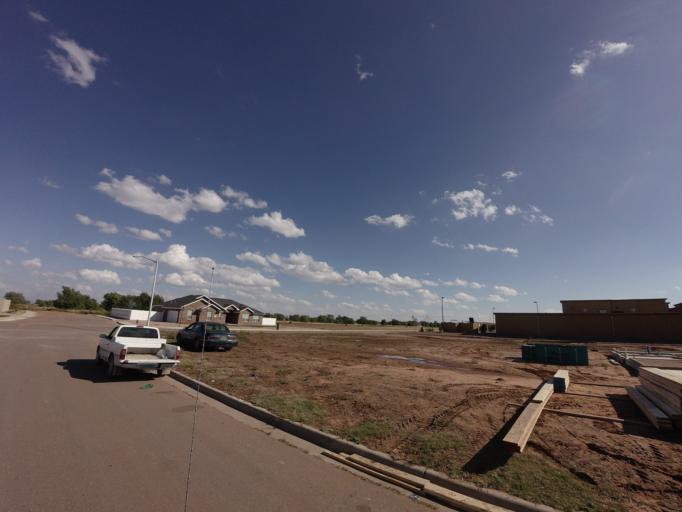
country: US
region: New Mexico
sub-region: Curry County
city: Clovis
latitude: 34.4363
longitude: -103.1741
